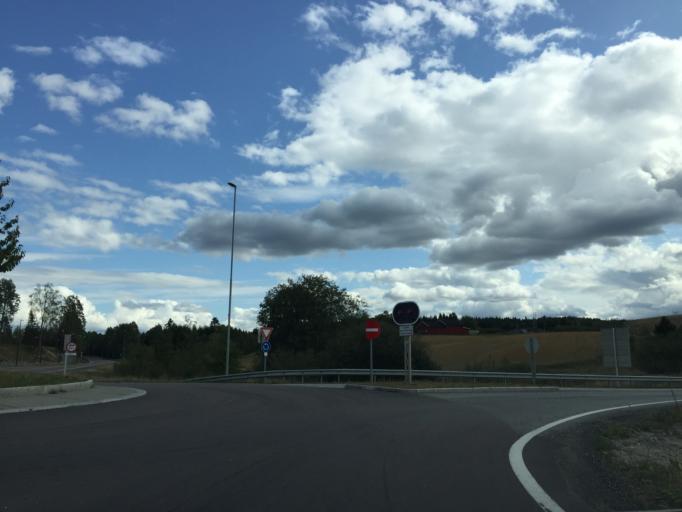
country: NO
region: Ostfold
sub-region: Hobol
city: Knappstad
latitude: 59.6211
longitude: 11.0051
